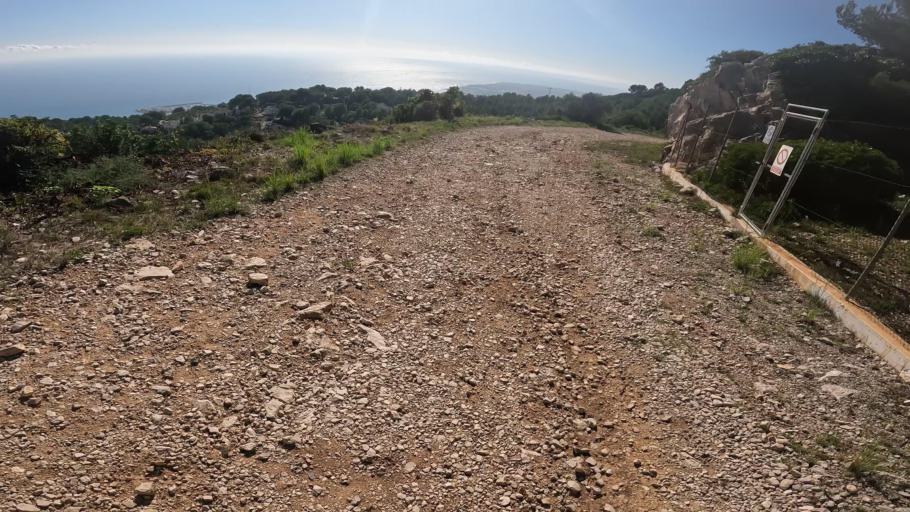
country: ES
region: Valencia
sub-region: Provincia de Castello
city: Alcoceber
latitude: 40.2678
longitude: 0.2729
